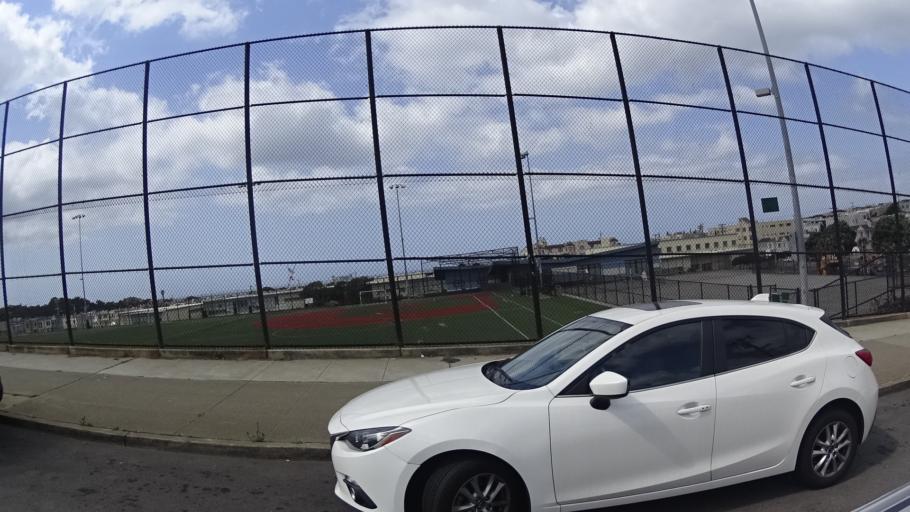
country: US
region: California
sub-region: San Mateo County
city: Daly City
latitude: 37.7376
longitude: -122.4979
